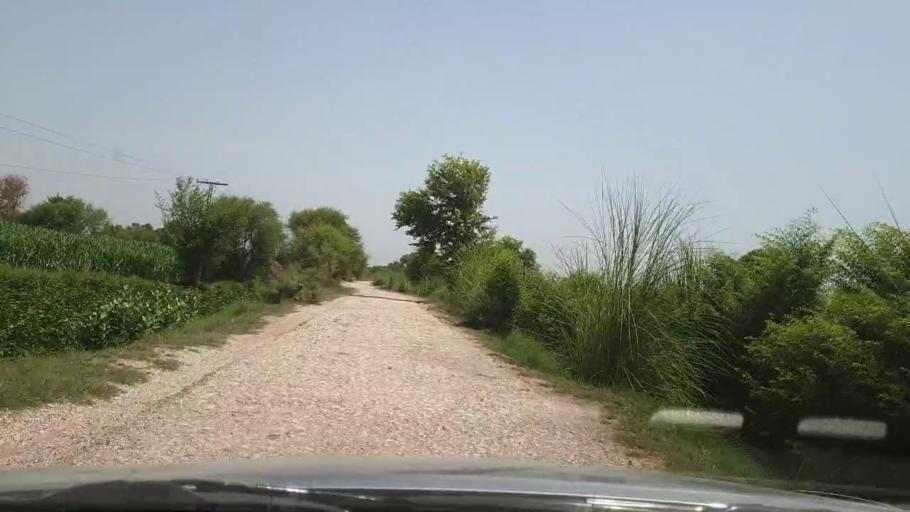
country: PK
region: Sindh
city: Pano Aqil
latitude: 27.8195
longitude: 69.2293
